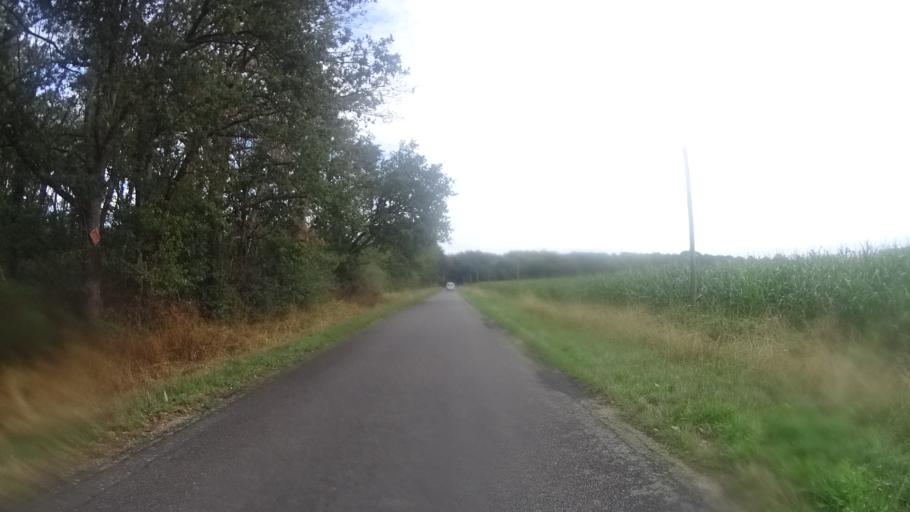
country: FR
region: Centre
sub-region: Departement du Loiret
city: Chateauneuf-sur-Loire
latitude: 47.8999
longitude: 2.2113
